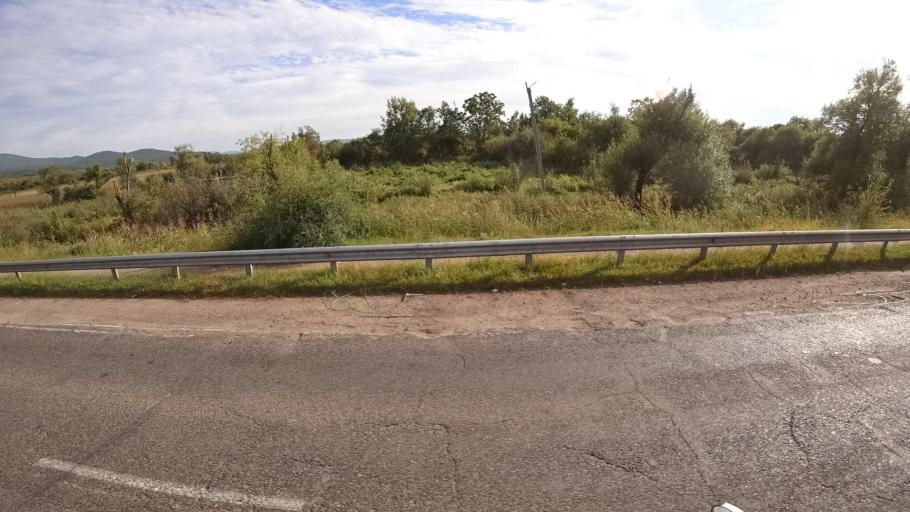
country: RU
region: Primorskiy
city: Dostoyevka
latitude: 44.2944
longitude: 133.4306
